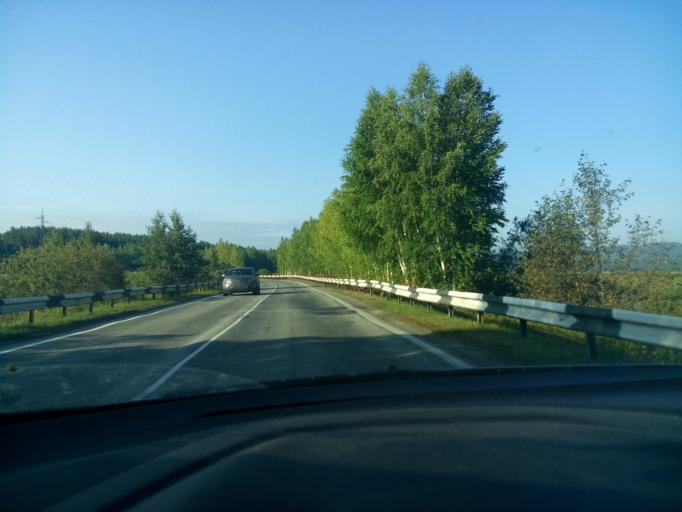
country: RU
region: Chelyabinsk
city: Kasli
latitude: 55.8701
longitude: 60.7002
